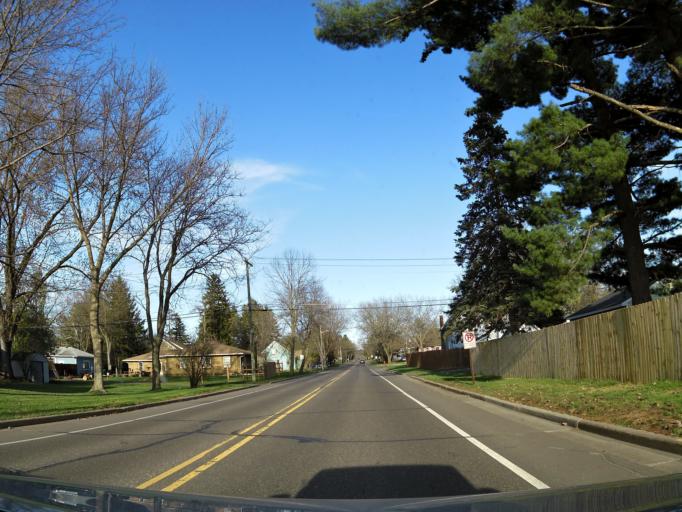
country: US
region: Wisconsin
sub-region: Pierce County
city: River Falls
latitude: 44.8626
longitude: -92.6334
